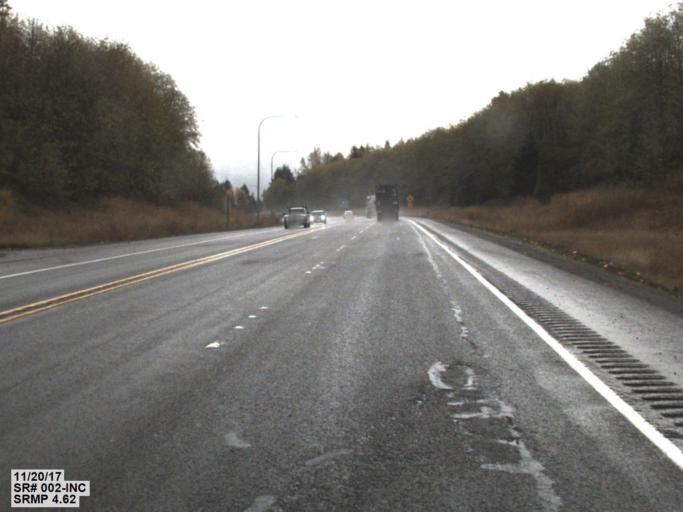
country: US
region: Washington
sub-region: Snohomish County
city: Fobes Hill
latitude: 47.9530
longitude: -122.1100
